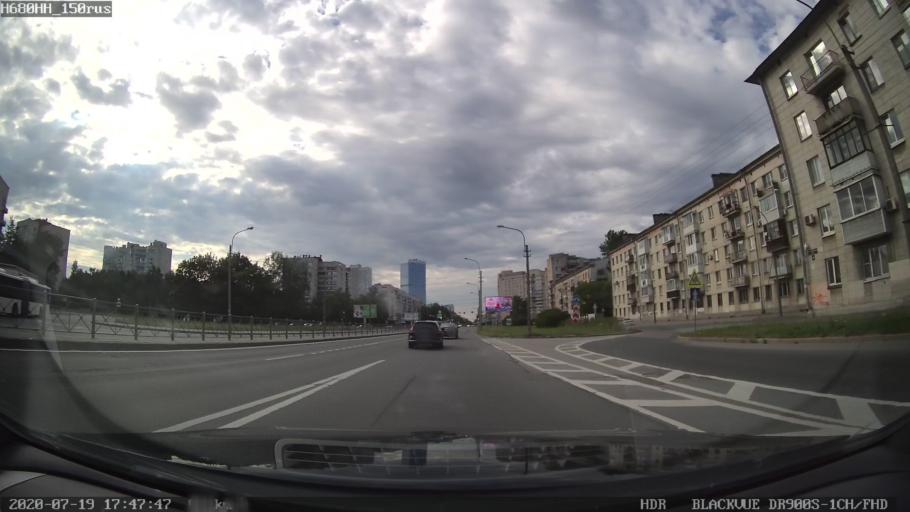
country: RU
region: St.-Petersburg
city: Kupchino
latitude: 59.8444
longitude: 30.3148
